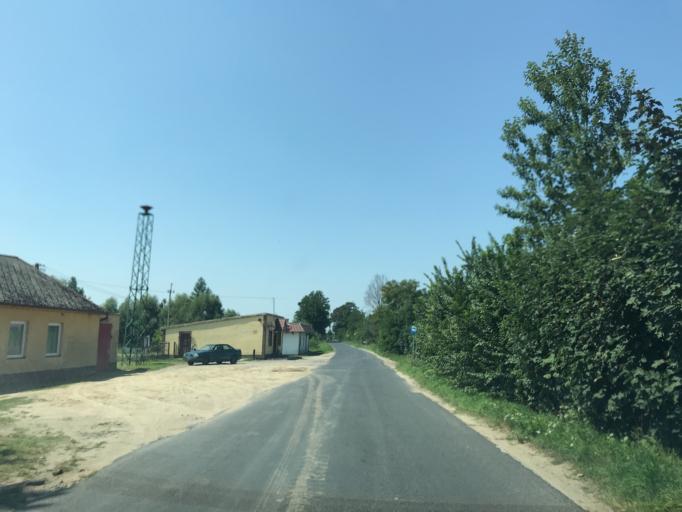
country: PL
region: Kujawsko-Pomorskie
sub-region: Powiat lipnowski
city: Chrostkowo
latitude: 52.9895
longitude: 19.2508
